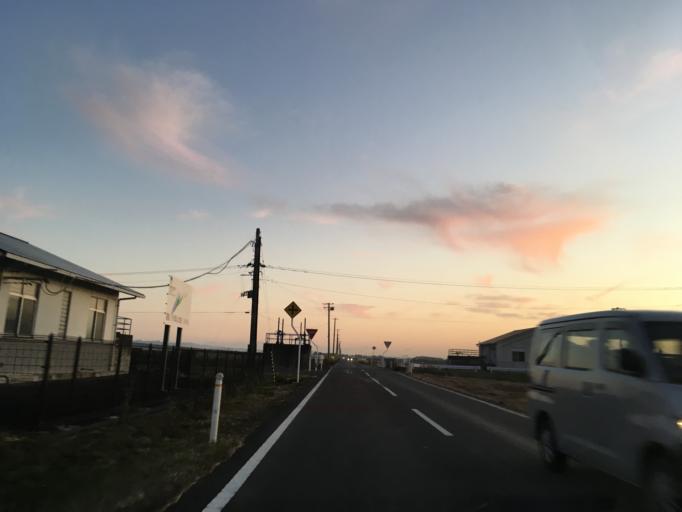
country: JP
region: Iwate
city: Ichinoseki
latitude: 38.7463
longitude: 141.2374
